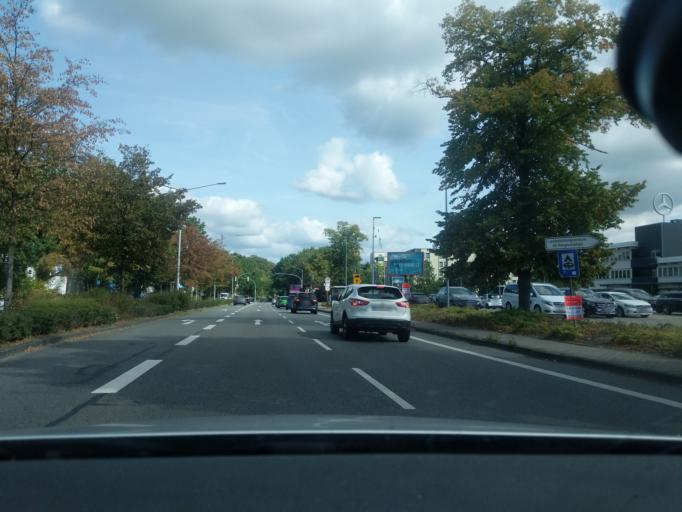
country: DE
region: Lower Saxony
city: Osnabrueck
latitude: 52.2648
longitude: 8.0064
